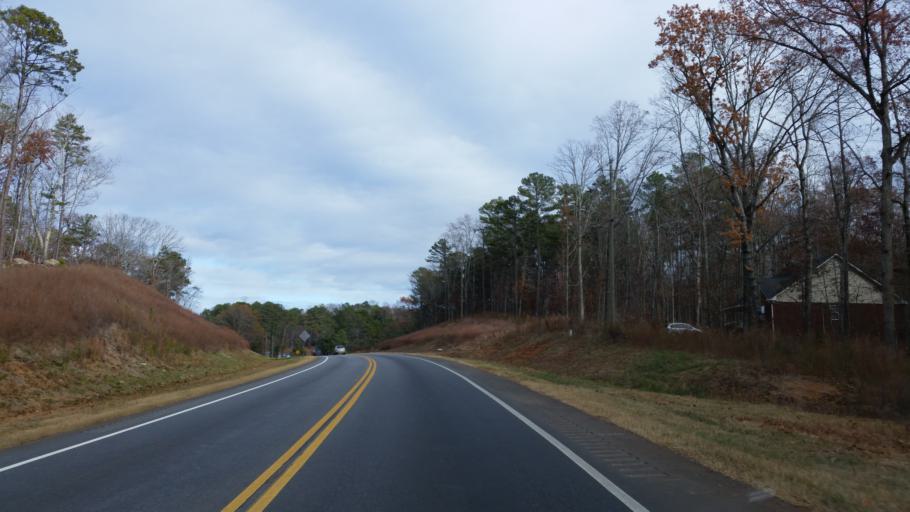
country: US
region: Georgia
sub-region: Bartow County
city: Emerson
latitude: 34.2205
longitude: -84.7173
